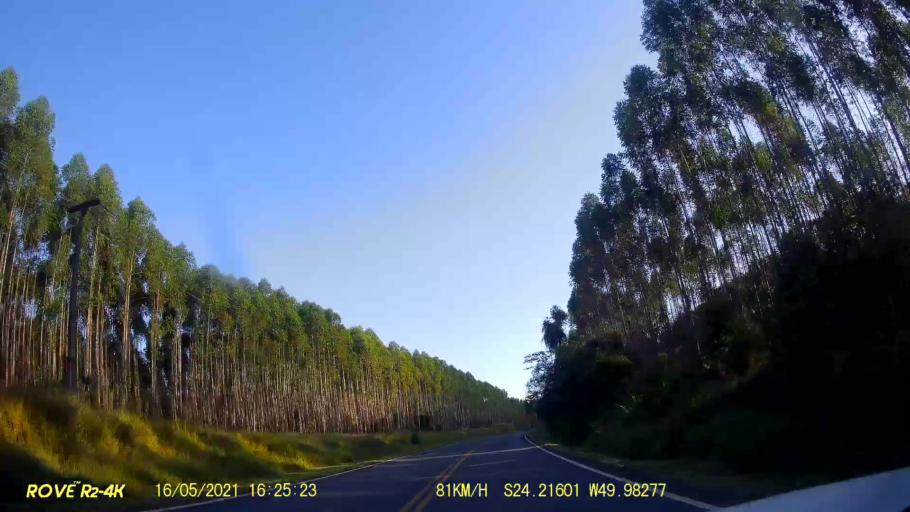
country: BR
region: Parana
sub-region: Jaguariaiva
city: Jaguariaiva
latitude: -24.2163
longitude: -49.9834
